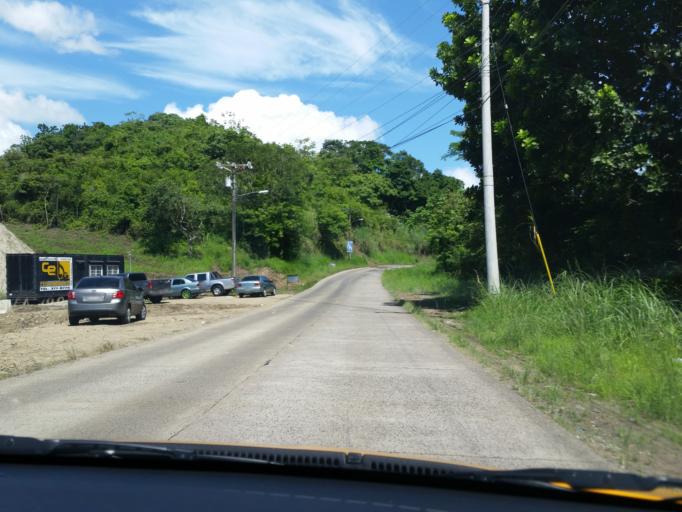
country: PA
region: Panama
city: San Miguelito
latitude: 9.0709
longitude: -79.4653
